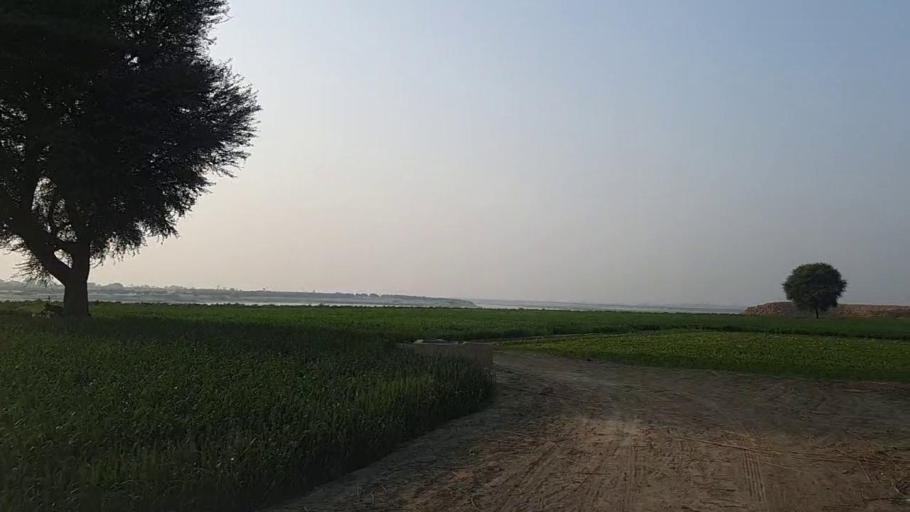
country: PK
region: Sindh
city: Sann
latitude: 26.1305
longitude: 68.1387
